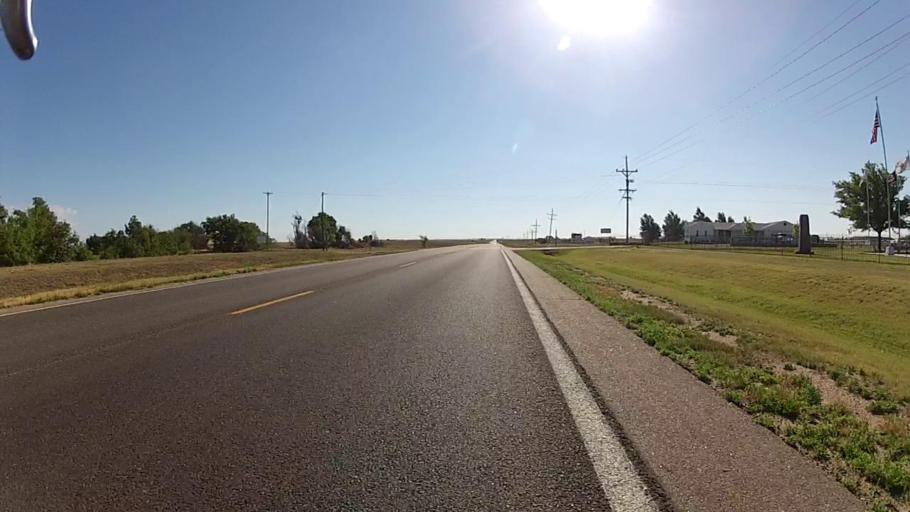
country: US
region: Kansas
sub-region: Haskell County
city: Sublette
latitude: 37.5463
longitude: -100.6166
